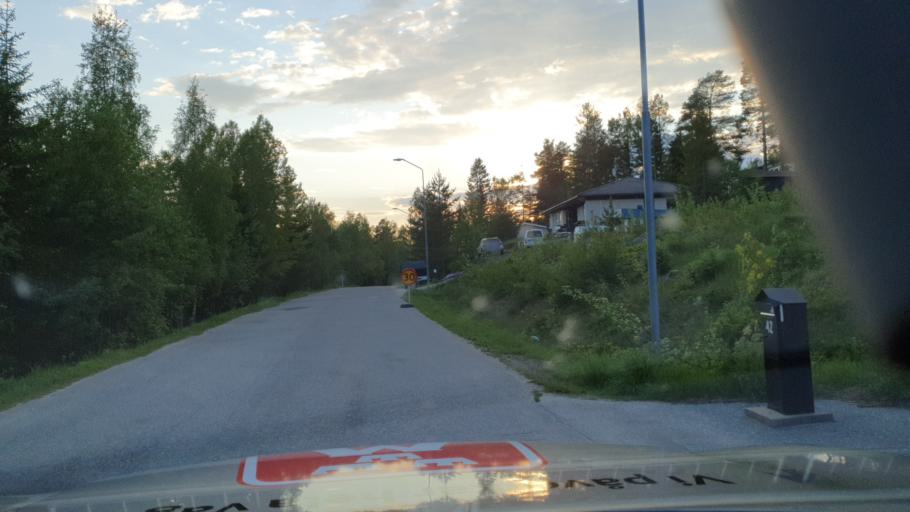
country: SE
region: Vaesternorrland
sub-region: OErnskoeldsviks Kommun
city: Ornskoldsvik
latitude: 63.2557
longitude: 18.6940
